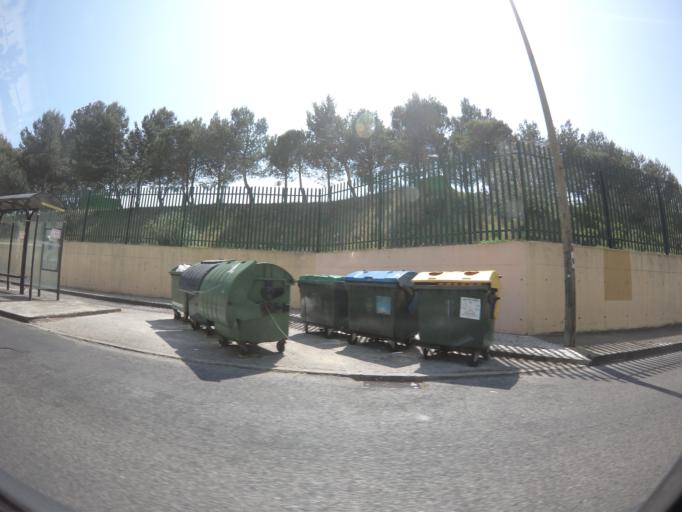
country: PT
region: Lisbon
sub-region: Loures
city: Moscavide
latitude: 38.7526
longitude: -9.1263
